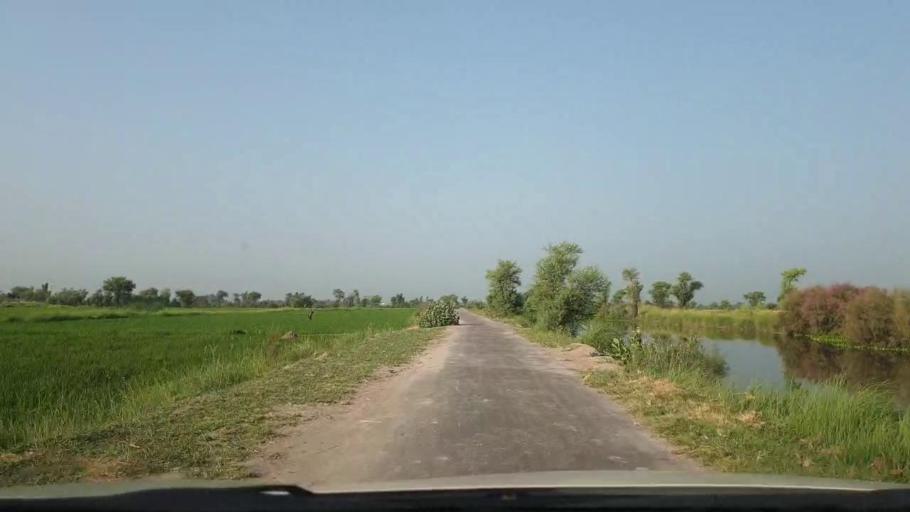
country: PK
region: Sindh
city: Larkana
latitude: 27.4960
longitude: 68.1711
